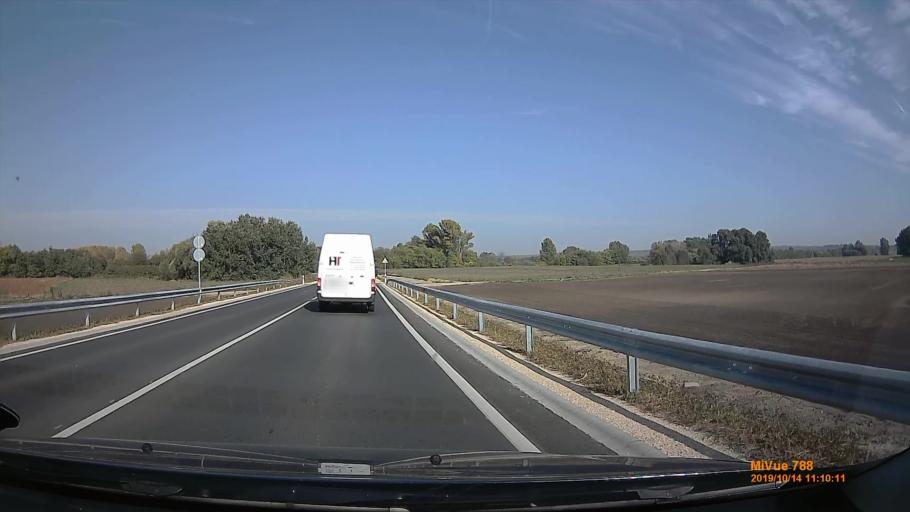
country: HU
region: Pest
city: Peteri
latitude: 47.3733
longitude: 19.4226
